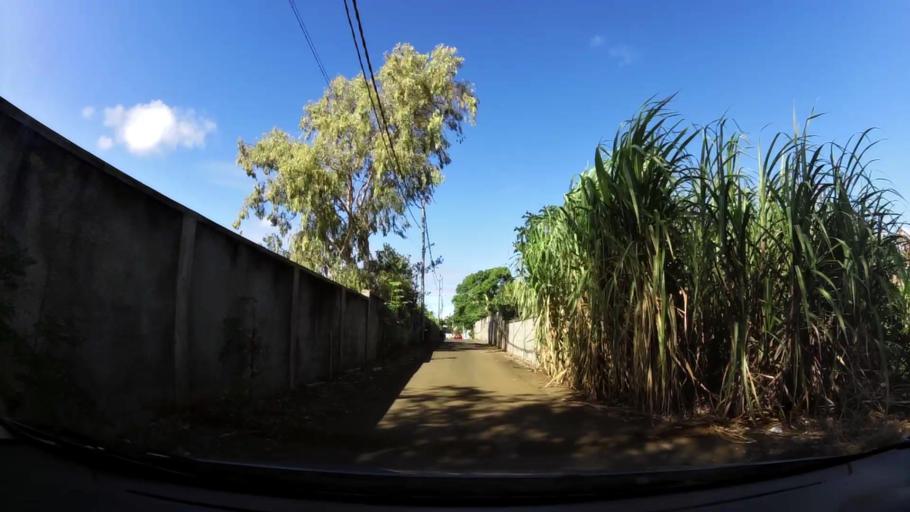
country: MU
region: Grand Port
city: Mahebourg
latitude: -20.4003
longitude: 57.6979
